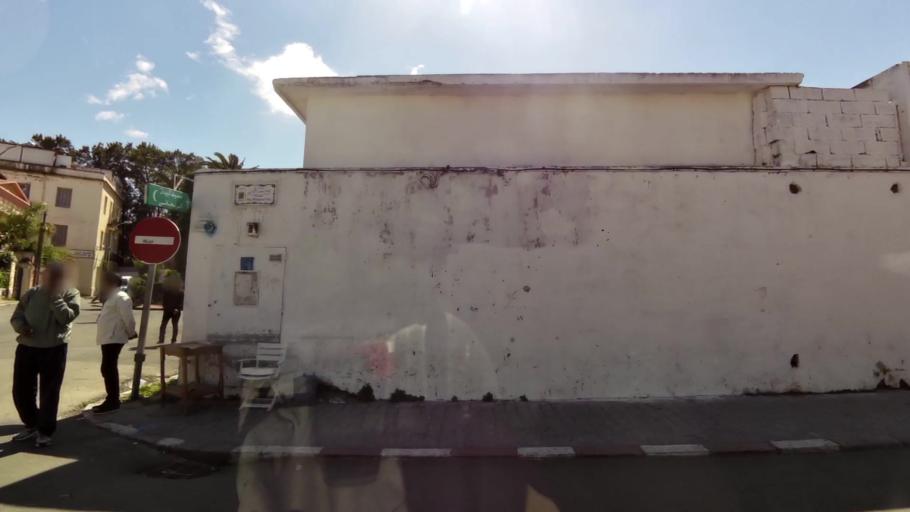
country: MA
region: Tanger-Tetouan
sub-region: Tanger-Assilah
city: Tangier
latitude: 35.7893
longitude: -5.8193
